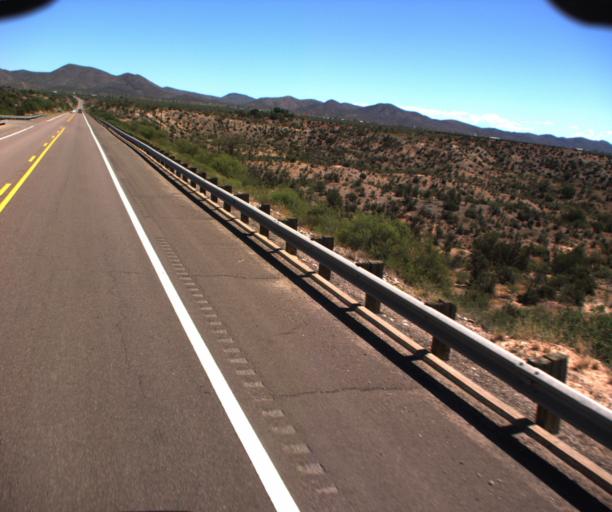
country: US
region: Arizona
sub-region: Gila County
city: Globe
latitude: 33.4124
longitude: -110.7394
